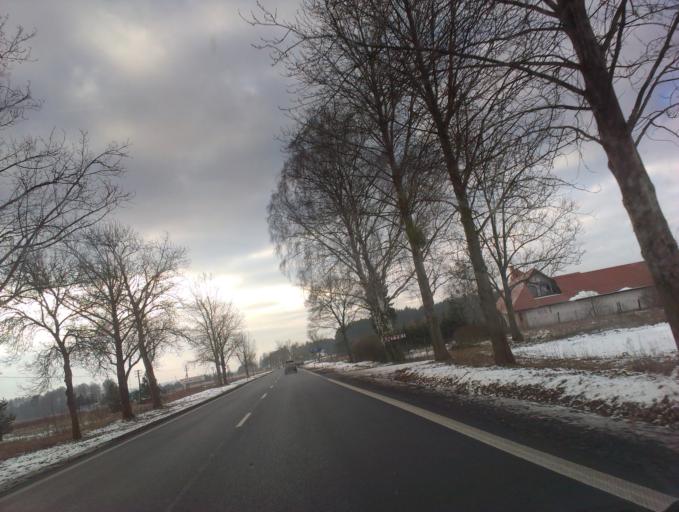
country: PL
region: Greater Poland Voivodeship
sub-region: Powiat zlotowski
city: Jastrowie
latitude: 53.4448
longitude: 16.8412
